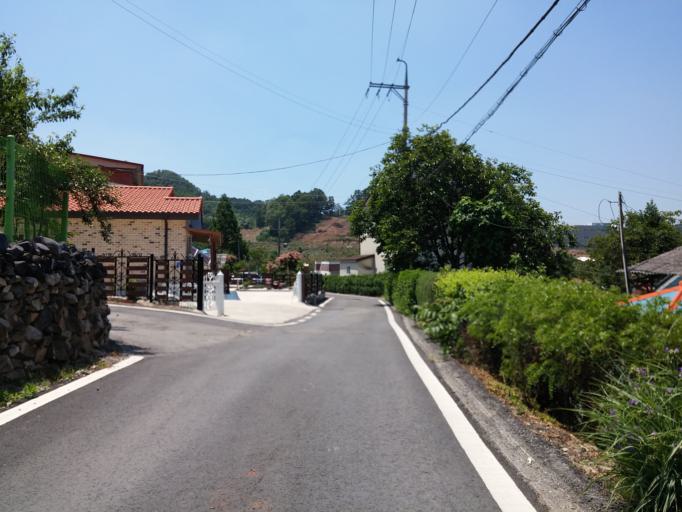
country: KR
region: Chungcheongbuk-do
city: Cheongju-si
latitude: 36.5550
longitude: 127.4366
